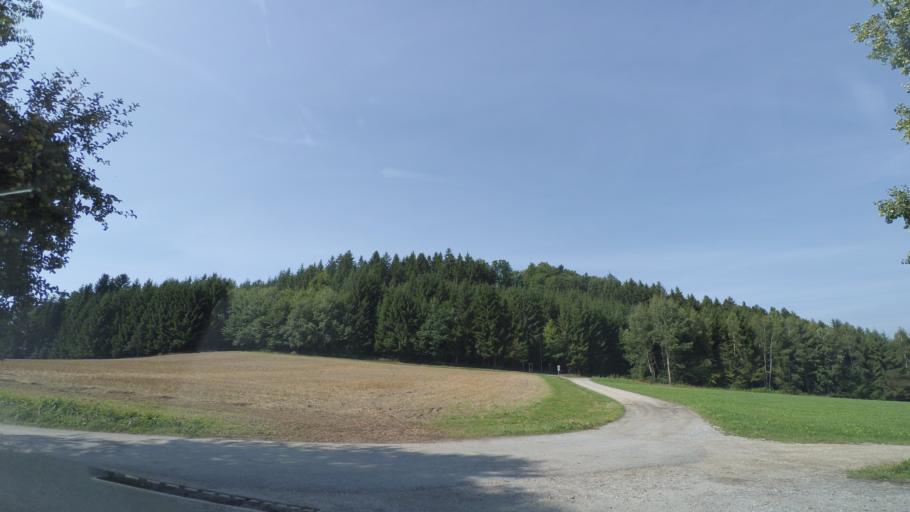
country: DE
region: Bavaria
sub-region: Lower Bavaria
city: Geiersthal
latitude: 49.0613
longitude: 12.9699
